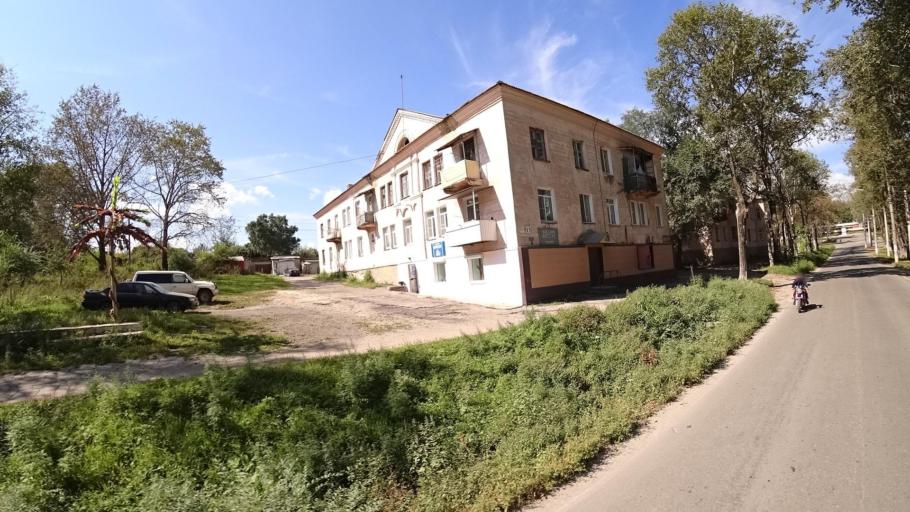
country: RU
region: Jewish Autonomous Oblast
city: Londoko
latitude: 49.0093
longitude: 131.8837
